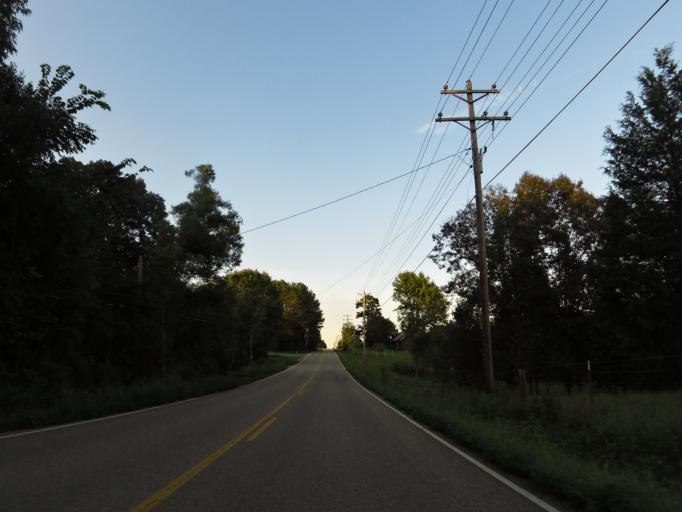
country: US
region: Tennessee
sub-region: Roane County
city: Rockwood
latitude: 35.7491
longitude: -84.6120
